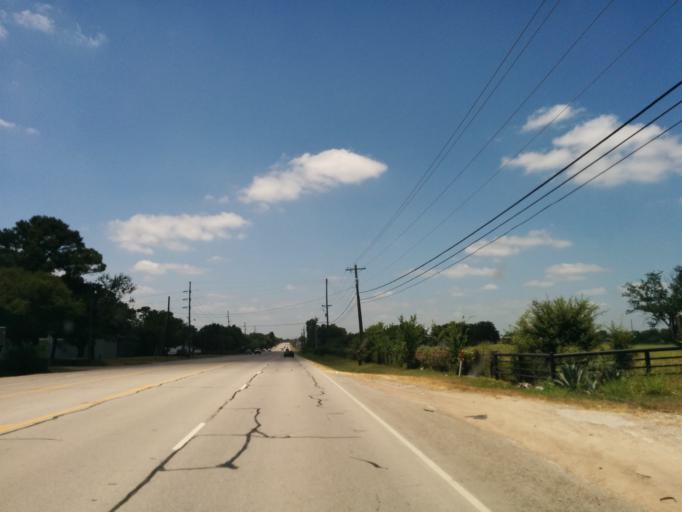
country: US
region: Texas
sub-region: Brazos County
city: Bryan
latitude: 30.7086
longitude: -96.3479
